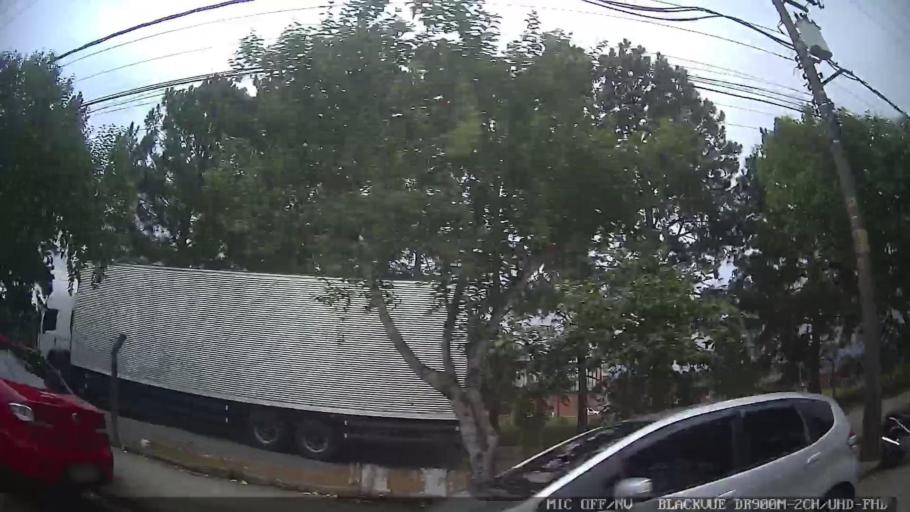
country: BR
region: Sao Paulo
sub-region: Mogi das Cruzes
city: Mogi das Cruzes
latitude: -23.5105
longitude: -46.1563
